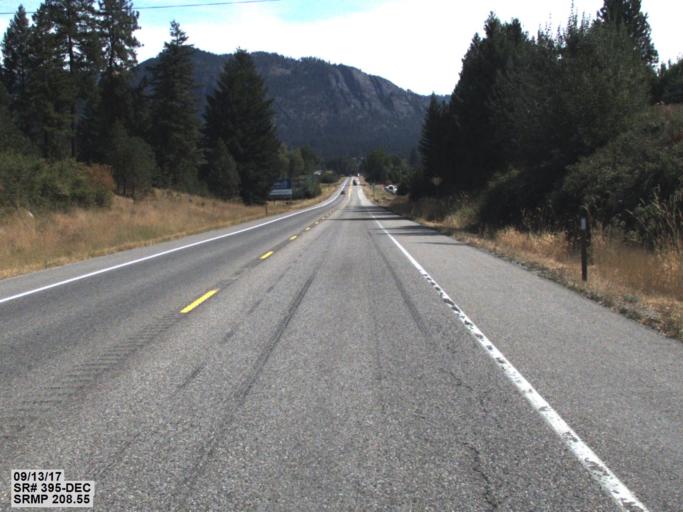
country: US
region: Washington
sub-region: Stevens County
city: Chewelah
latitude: 48.2904
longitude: -117.7324
